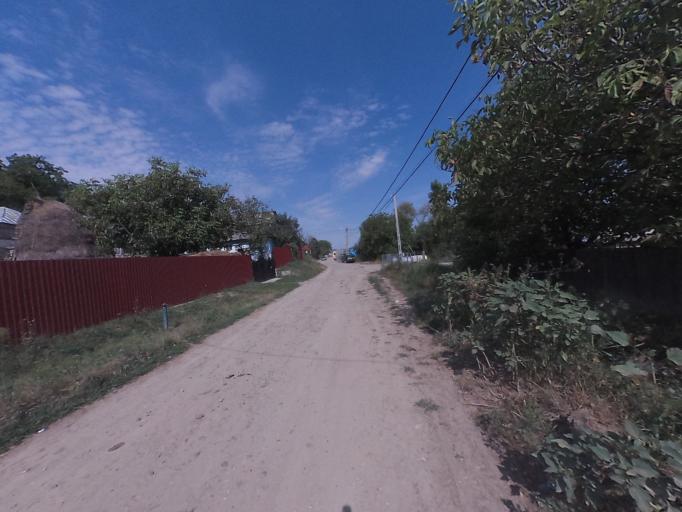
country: RO
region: Vaslui
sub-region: Comuna Osesti
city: Buda
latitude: 46.7631
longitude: 27.4088
